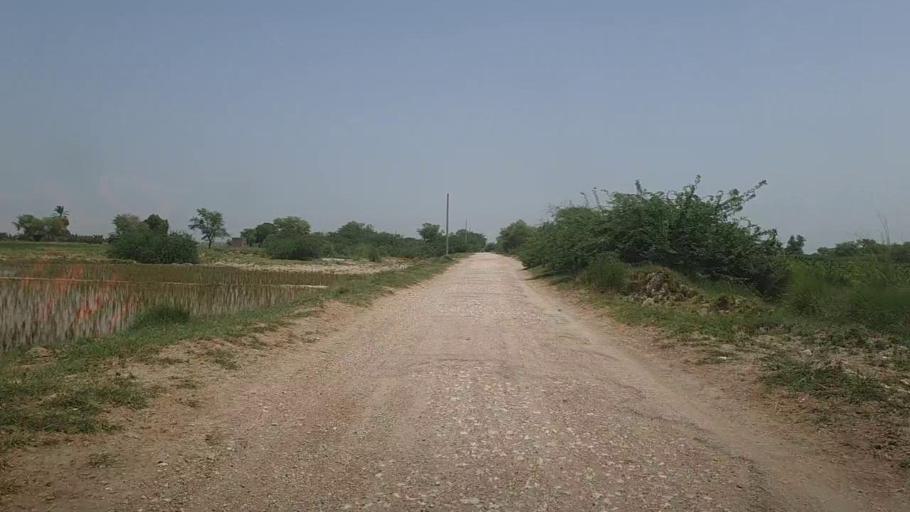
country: PK
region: Sindh
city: Pad Idan
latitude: 26.8447
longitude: 68.2815
